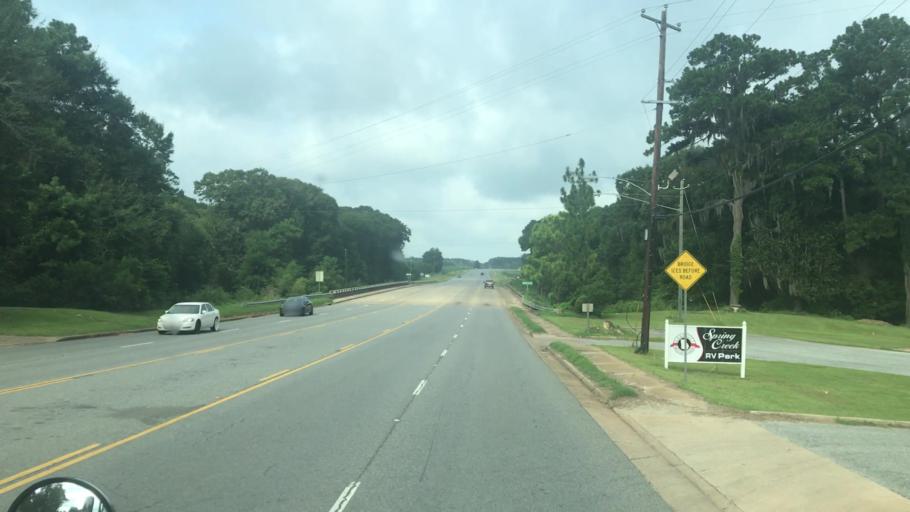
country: US
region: Georgia
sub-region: Miller County
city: Colquitt
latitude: 31.1712
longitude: -84.7413
